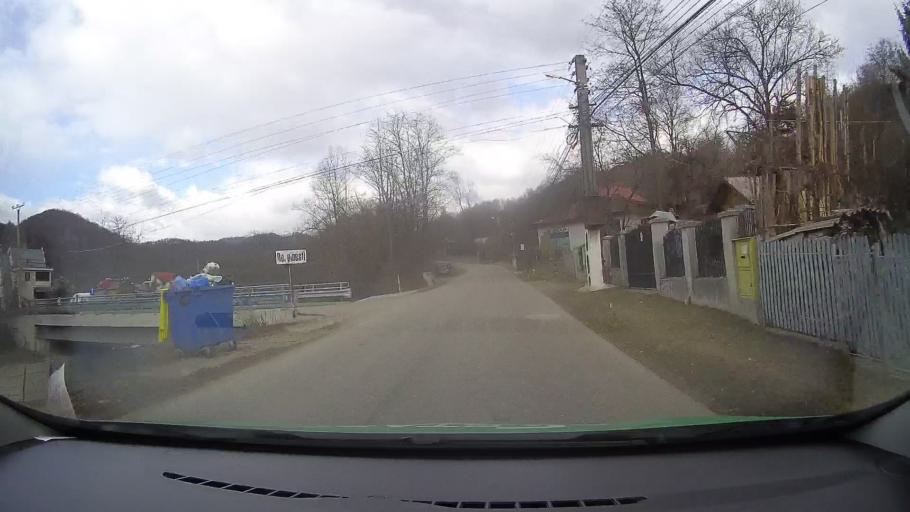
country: RO
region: Dambovita
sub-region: Comuna Visinesti
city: Visinesti
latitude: 45.1018
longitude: 25.5640
